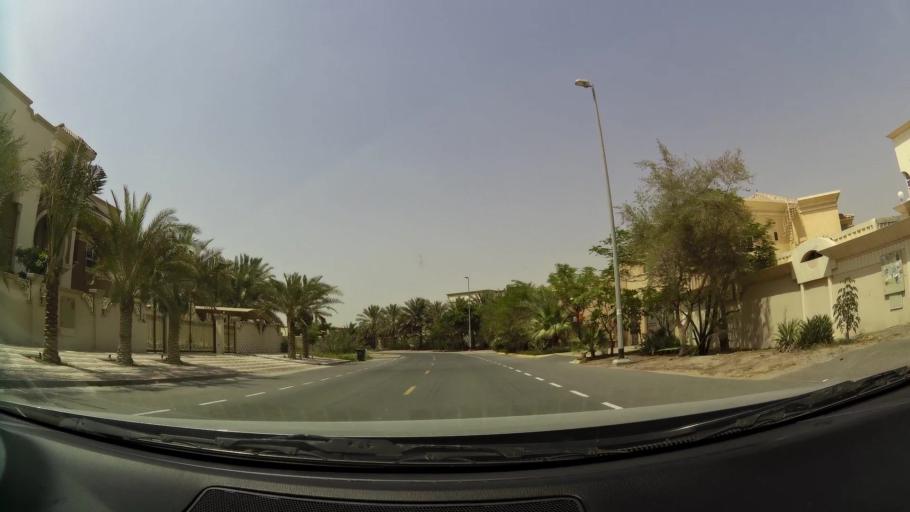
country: AE
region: Ash Shariqah
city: Sharjah
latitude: 25.2464
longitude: 55.4297
